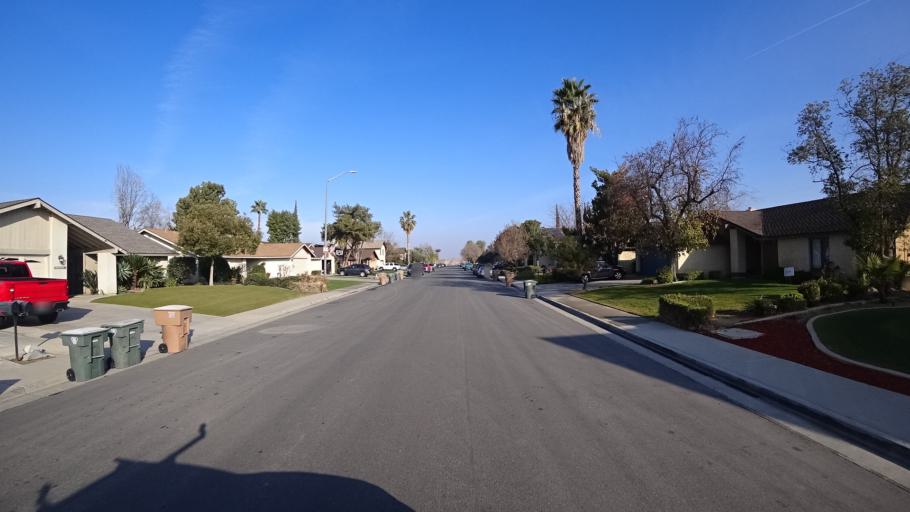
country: US
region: California
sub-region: Kern County
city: Oildale
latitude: 35.4047
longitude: -118.9325
